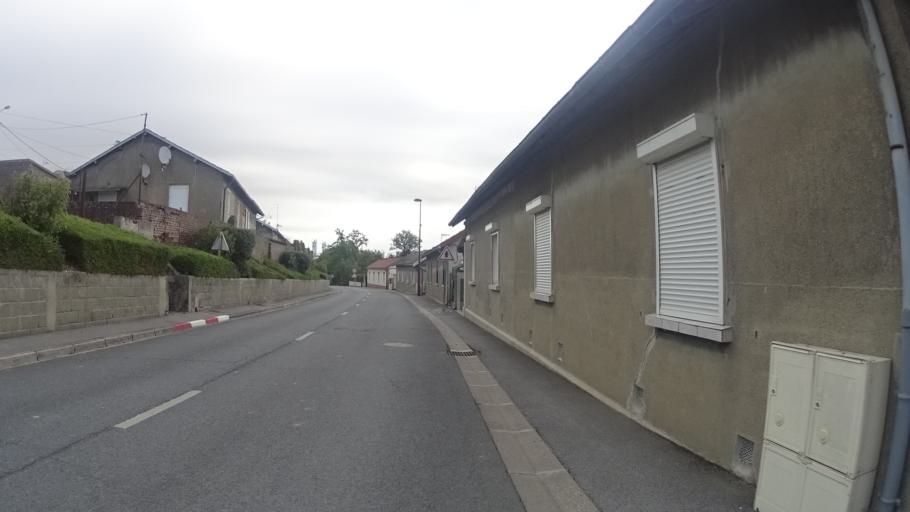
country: FR
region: Picardie
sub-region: Departement de l'Aisne
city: Origny-Sainte-Benoite
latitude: 49.8336
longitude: 3.4722
